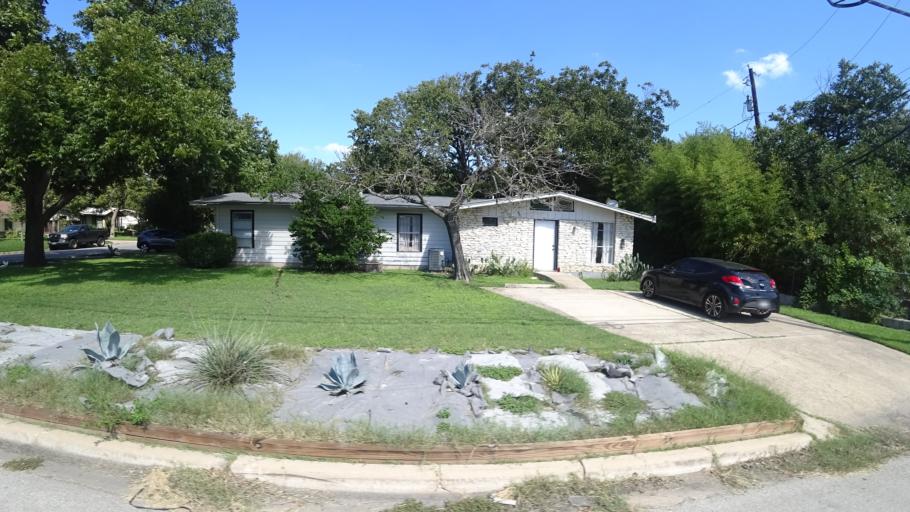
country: US
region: Texas
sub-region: Travis County
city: Austin
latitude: 30.3139
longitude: -97.6877
